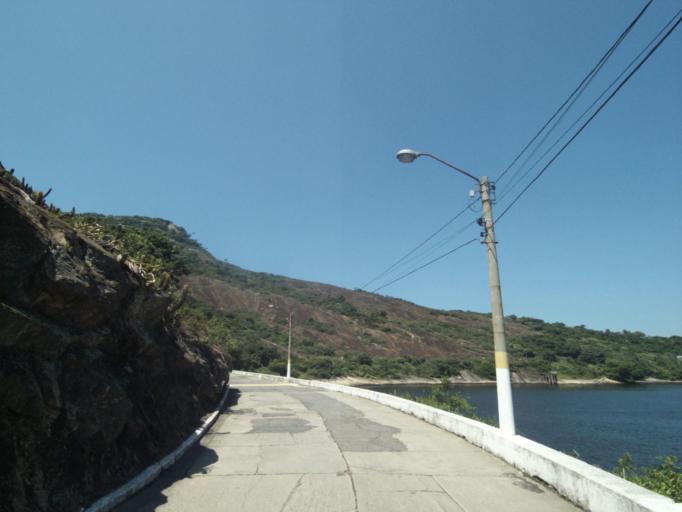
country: BR
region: Rio de Janeiro
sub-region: Niteroi
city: Niteroi
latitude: -22.9329
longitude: -43.1271
